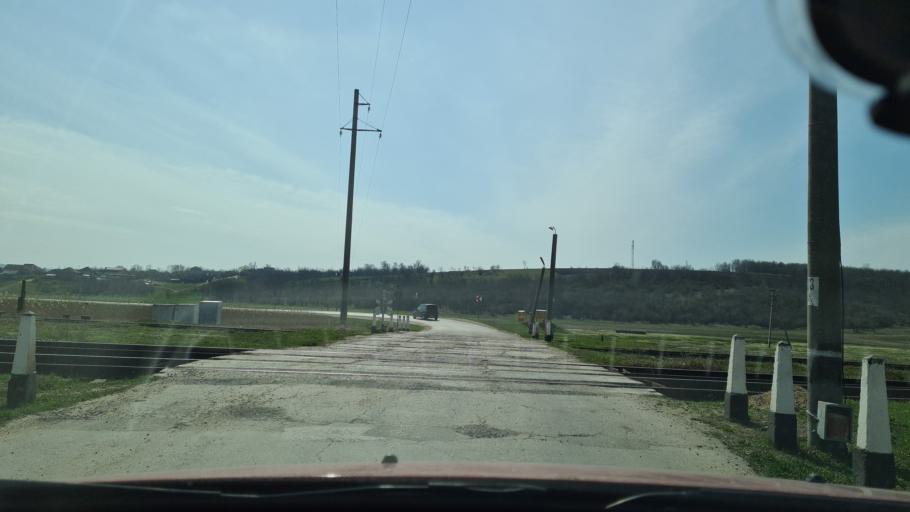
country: MD
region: Ungheni
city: Ungheni
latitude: 47.3207
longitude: 27.8882
